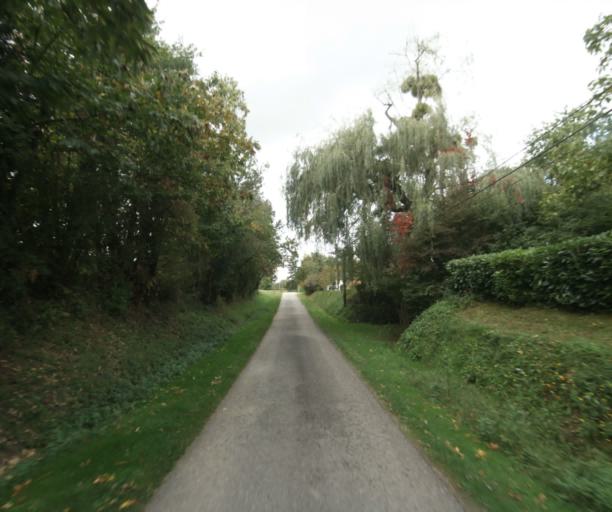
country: FR
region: Midi-Pyrenees
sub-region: Departement du Gers
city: Eauze
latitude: 43.9306
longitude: 0.0811
